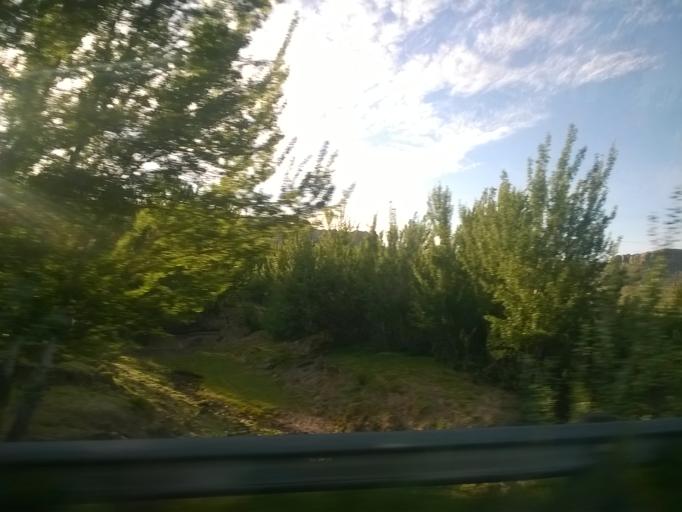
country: LS
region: Berea
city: Teyateyaneng
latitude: -29.1605
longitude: 27.6533
